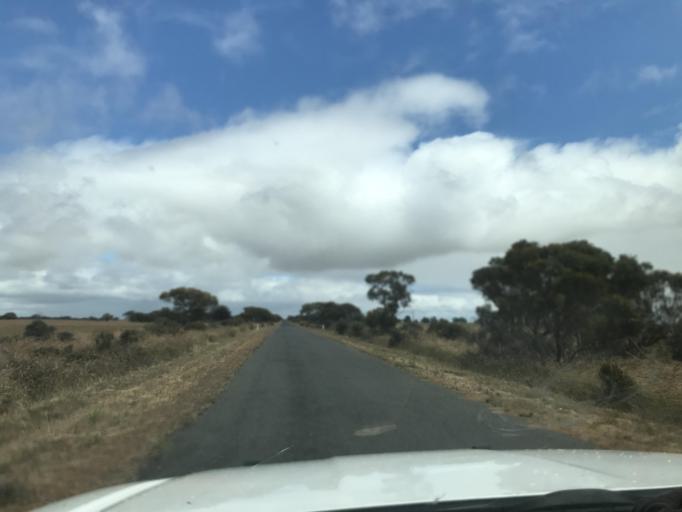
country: AU
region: South Australia
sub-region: Tatiara
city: Bordertown
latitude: -36.1375
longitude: 141.2027
